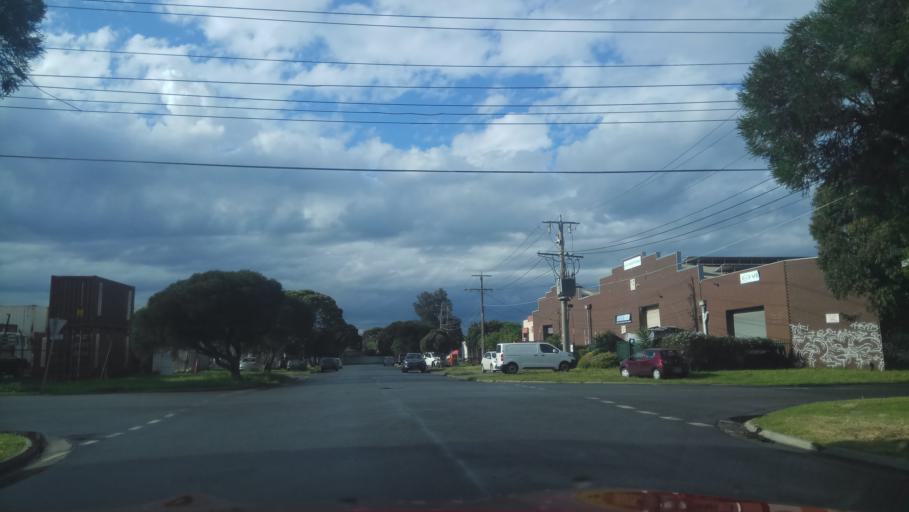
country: AU
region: Victoria
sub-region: Brimbank
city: Brooklyn
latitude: -37.8236
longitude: 144.8323
